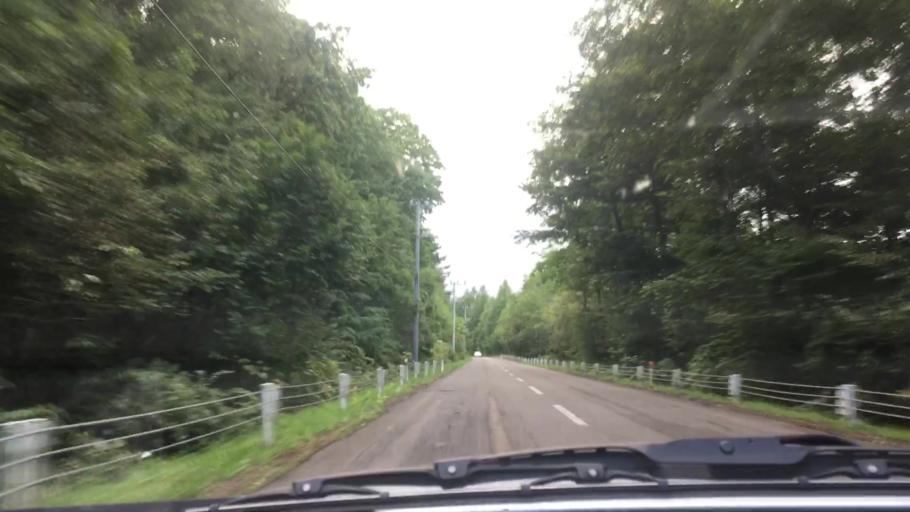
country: JP
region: Hokkaido
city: Otofuke
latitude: 43.1460
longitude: 142.8743
